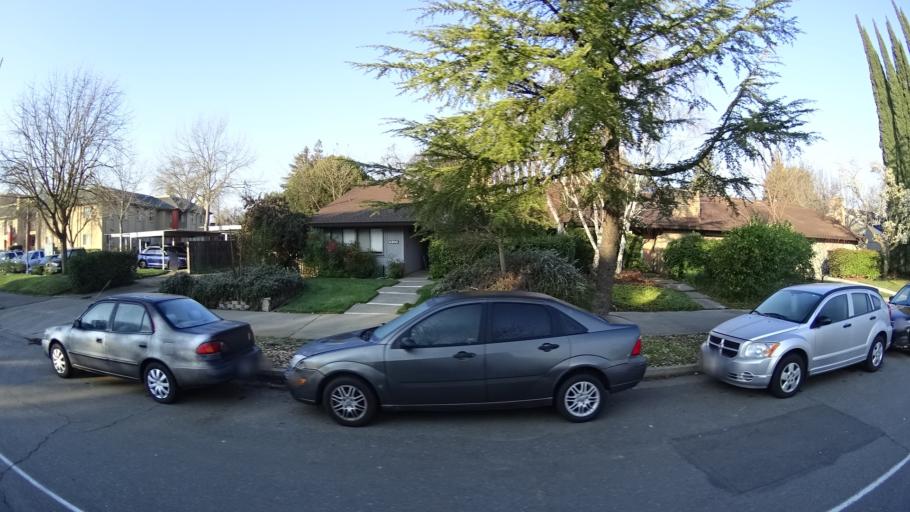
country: US
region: California
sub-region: Yolo County
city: Davis
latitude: 38.5545
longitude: -121.7878
